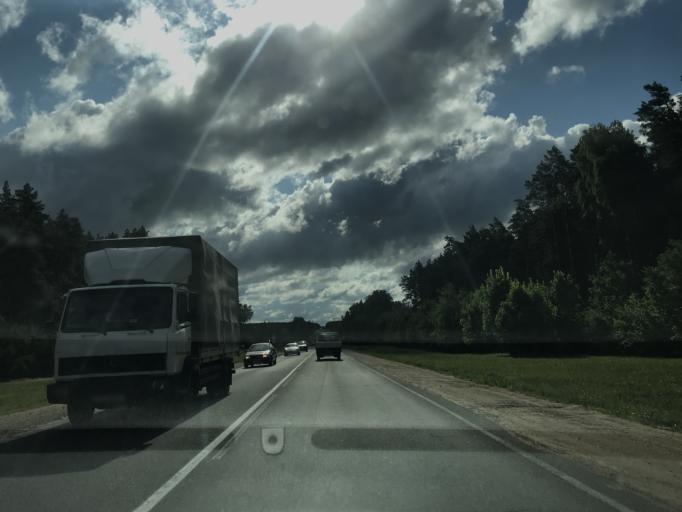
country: BY
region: Minsk
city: Borovlyany
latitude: 53.9676
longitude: 27.6339
